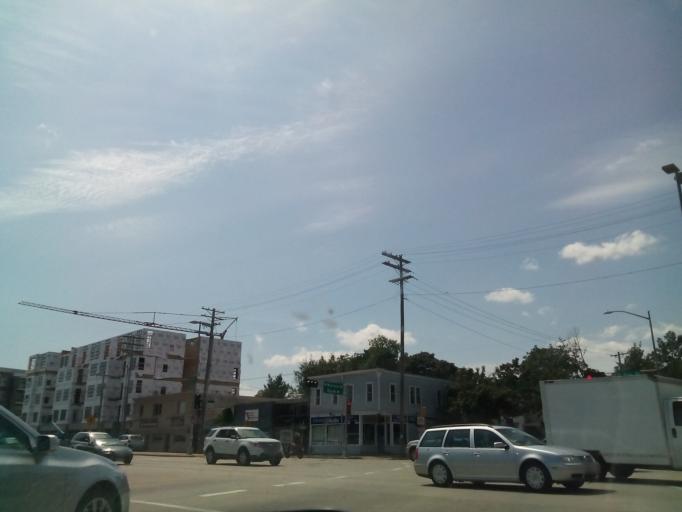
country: US
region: Wisconsin
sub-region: Dane County
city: Madison
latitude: 43.0634
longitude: -89.4005
